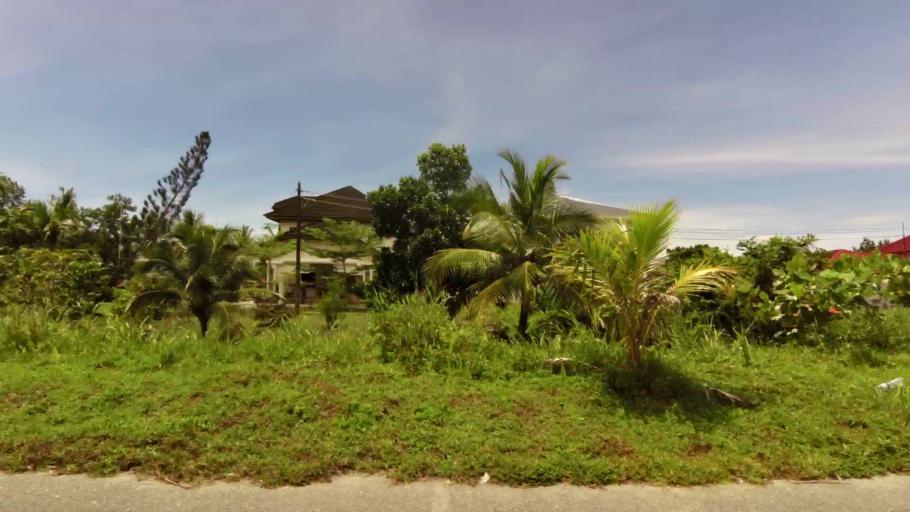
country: BN
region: Belait
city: Kuala Belait
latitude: 4.5836
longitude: 114.2484
